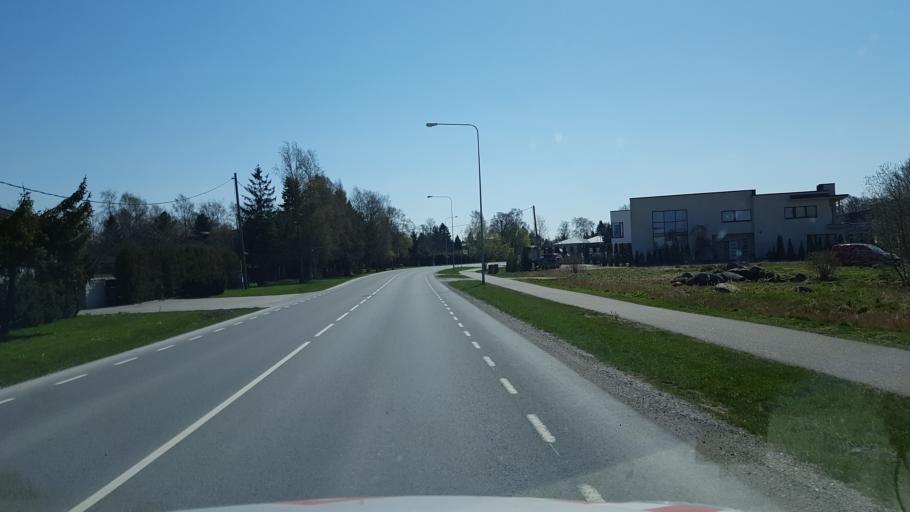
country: EE
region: Harju
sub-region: Viimsi vald
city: Rummu
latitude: 59.5448
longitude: 24.7951
